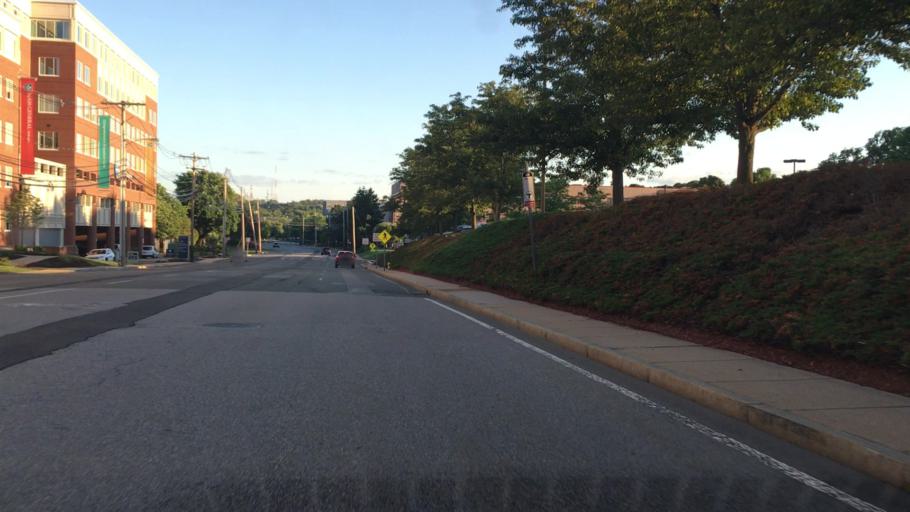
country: US
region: Massachusetts
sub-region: Middlesex County
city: Waltham
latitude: 42.3966
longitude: -71.2641
